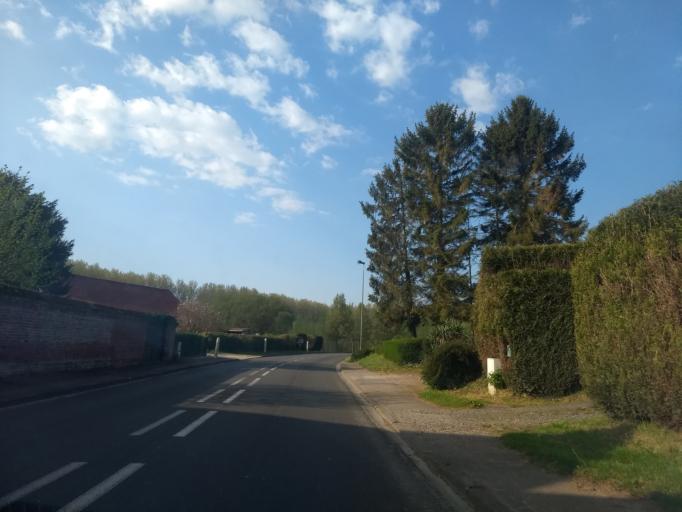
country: FR
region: Picardie
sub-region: Departement de la Somme
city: Corbie
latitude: 50.0011
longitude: 2.4710
